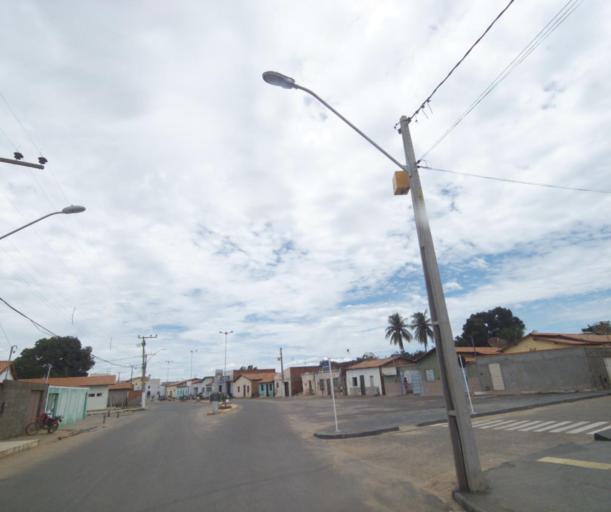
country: BR
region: Bahia
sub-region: Carinhanha
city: Carinhanha
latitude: -14.3340
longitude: -43.7713
